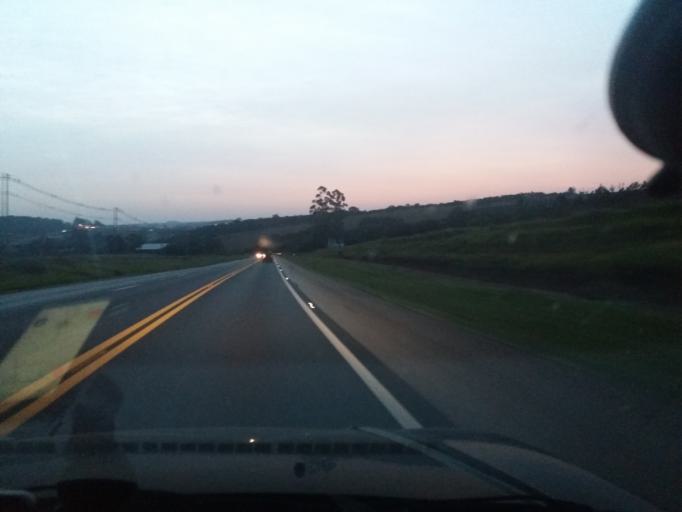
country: BR
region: Sao Paulo
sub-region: Itapeva
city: Itapeva
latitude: -23.9778
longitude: -48.8359
